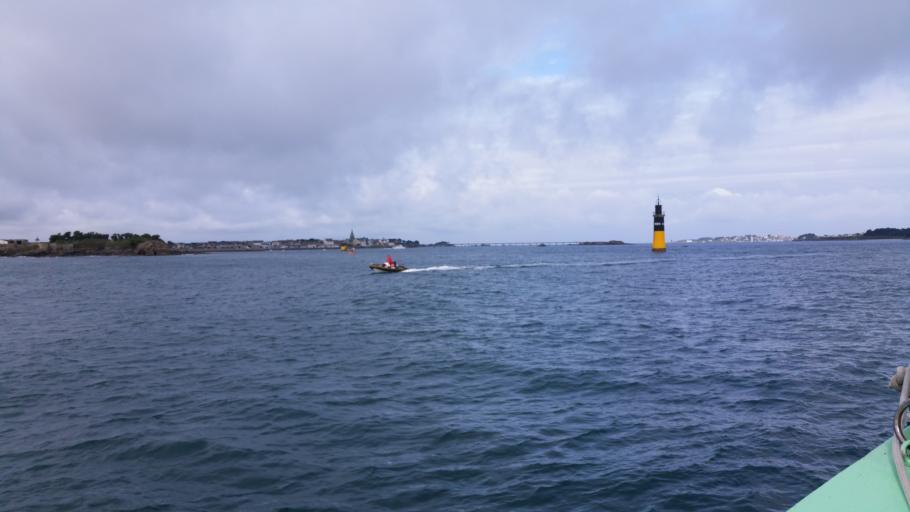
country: FR
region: Brittany
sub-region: Departement du Finistere
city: Roscoff
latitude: 48.7289
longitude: -3.9643
